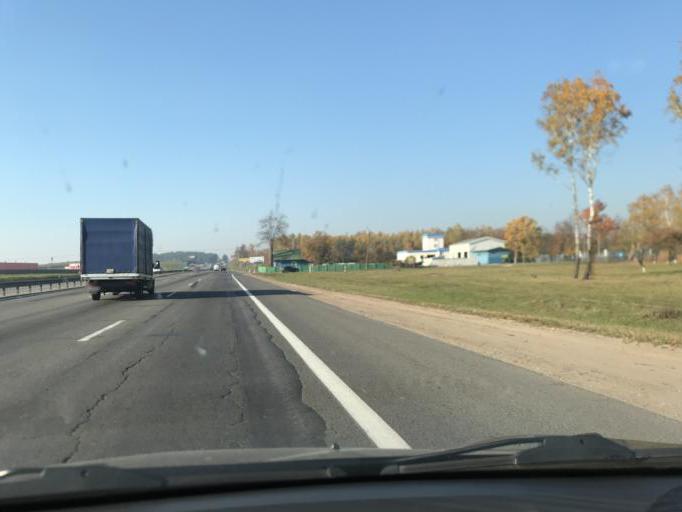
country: BY
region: Minsk
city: Pryvol'ny
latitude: 53.8087
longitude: 27.7857
